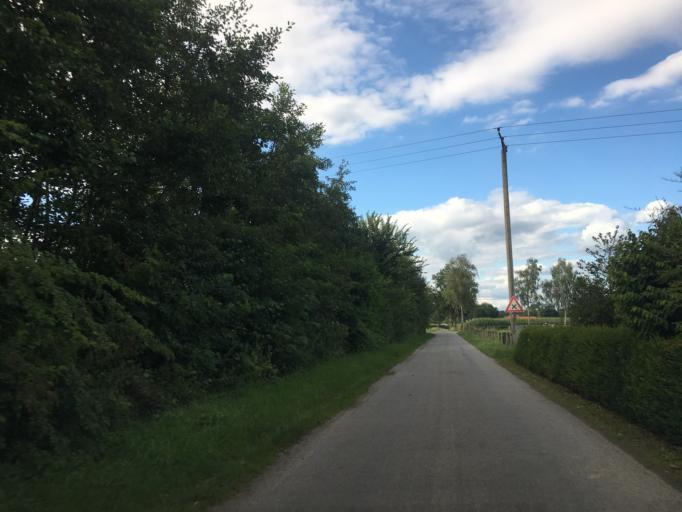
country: DE
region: North Rhine-Westphalia
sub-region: Regierungsbezirk Munster
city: Nordkirchen
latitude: 51.7517
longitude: 7.4921
